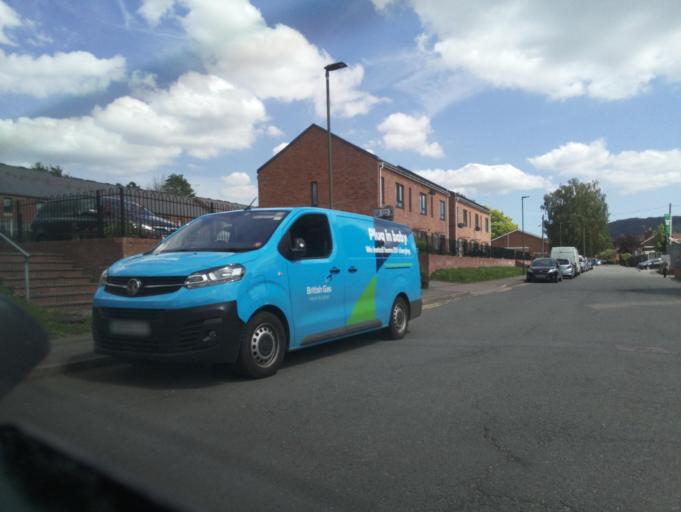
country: GB
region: England
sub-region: Herefordshire
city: Ross on Wye
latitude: 51.9185
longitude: -2.5855
